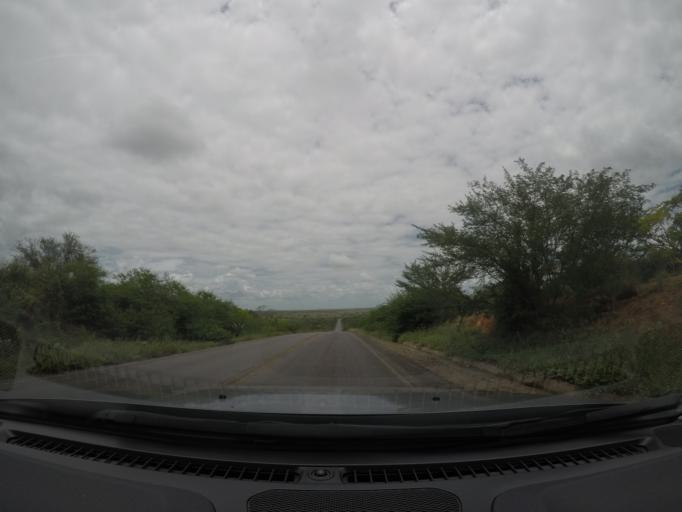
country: BR
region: Bahia
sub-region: Itaberaba
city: Itaberaba
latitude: -12.4954
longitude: -40.2388
